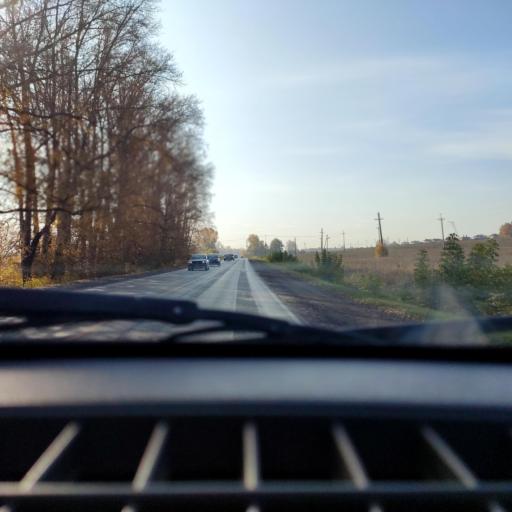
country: RU
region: Bashkortostan
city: Avdon
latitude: 54.7300
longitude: 55.8052
